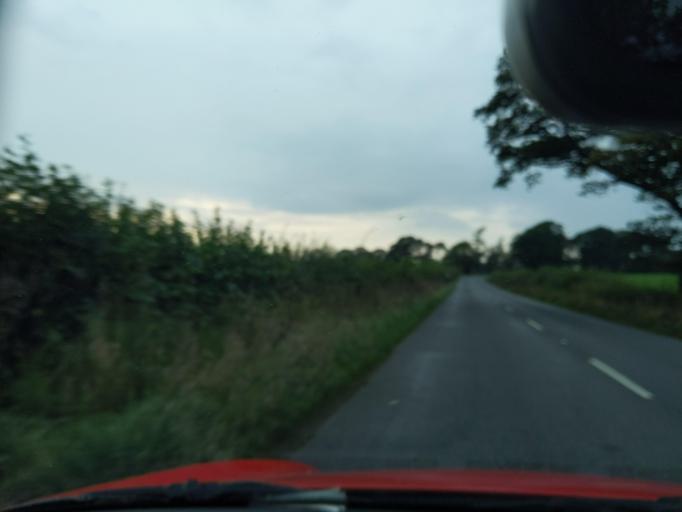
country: GB
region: England
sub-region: Devon
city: Okehampton
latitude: 50.7988
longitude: -4.0507
